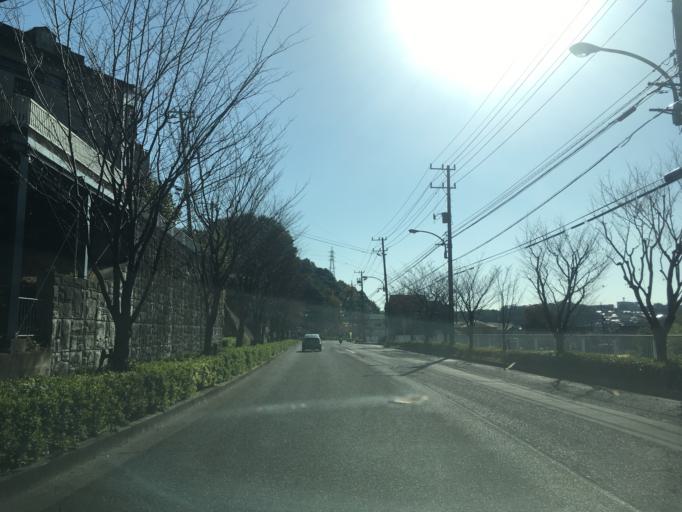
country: JP
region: Tokyo
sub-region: Machida-shi
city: Machida
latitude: 35.5880
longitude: 139.4195
